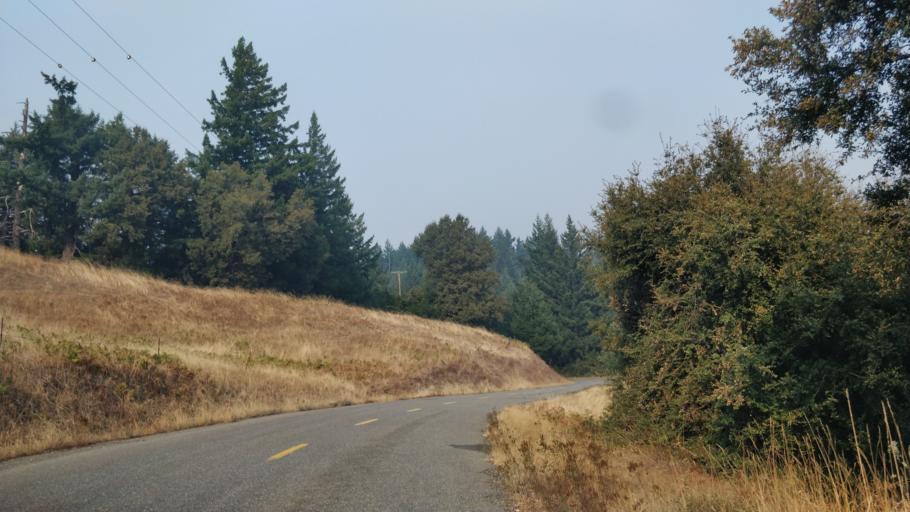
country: US
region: California
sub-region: Humboldt County
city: Rio Dell
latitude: 40.2808
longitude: -124.0665
